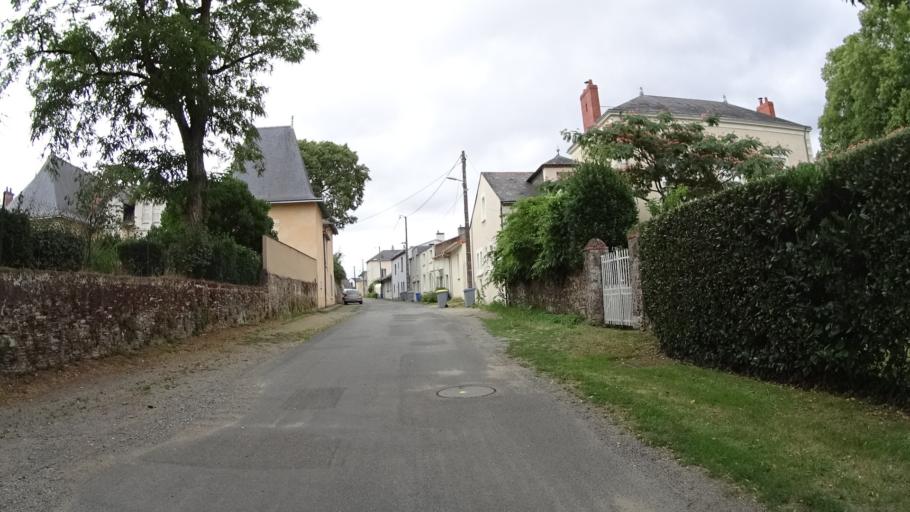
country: FR
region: Pays de la Loire
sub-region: Departement de la Loire-Atlantique
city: Thouare-sur-Loire
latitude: 47.2615
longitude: -1.4380
